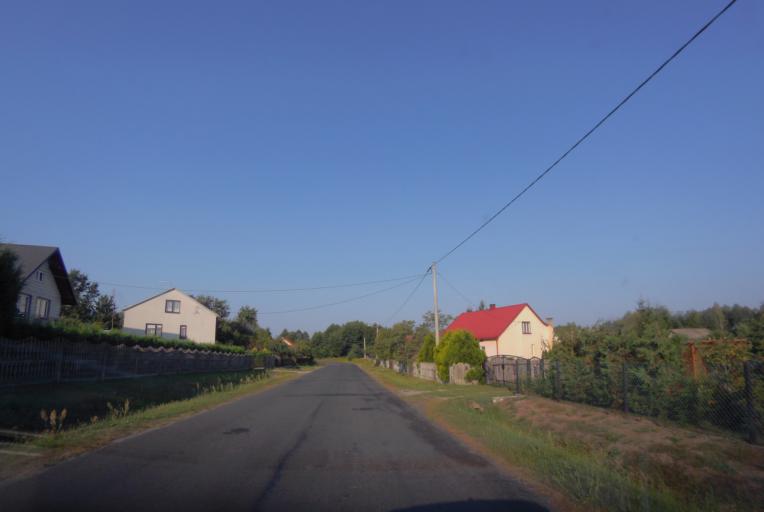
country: PL
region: Subcarpathian Voivodeship
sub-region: Powiat nizanski
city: Harasiuki
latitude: 50.5430
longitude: 22.5324
